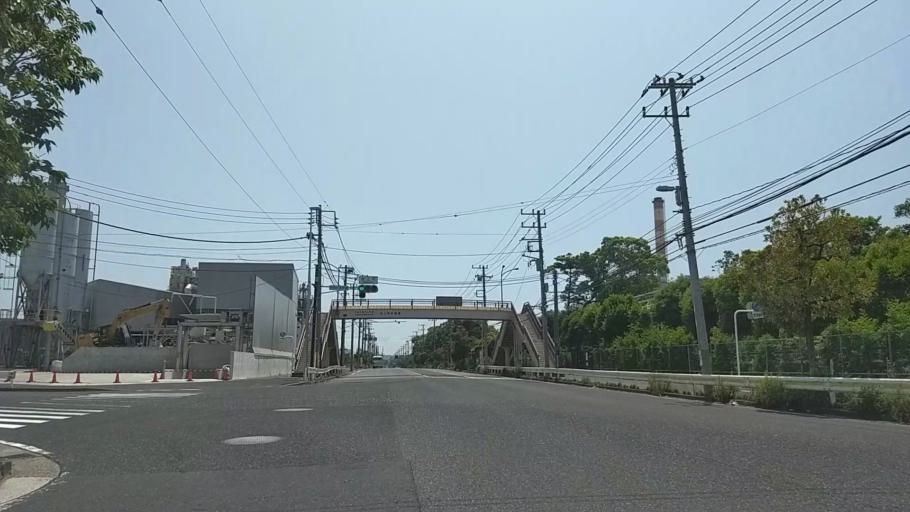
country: JP
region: Kanagawa
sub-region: Kawasaki-shi
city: Kawasaki
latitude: 35.5168
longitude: 139.7364
